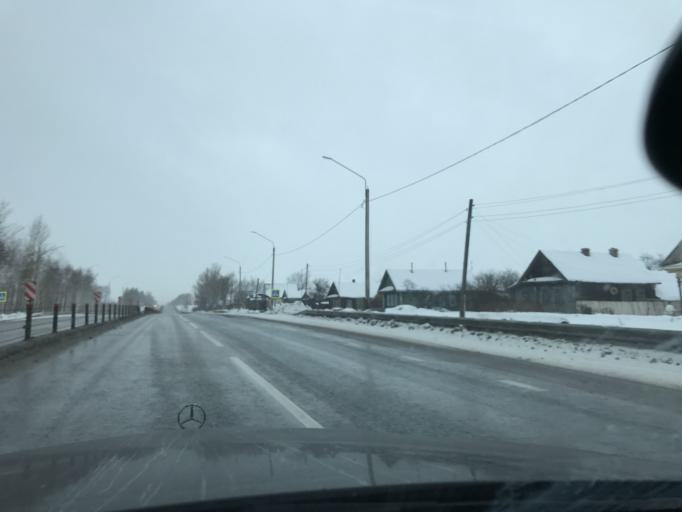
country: RU
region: Vladimir
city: Novovyazniki
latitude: 56.1823
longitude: 42.4049
